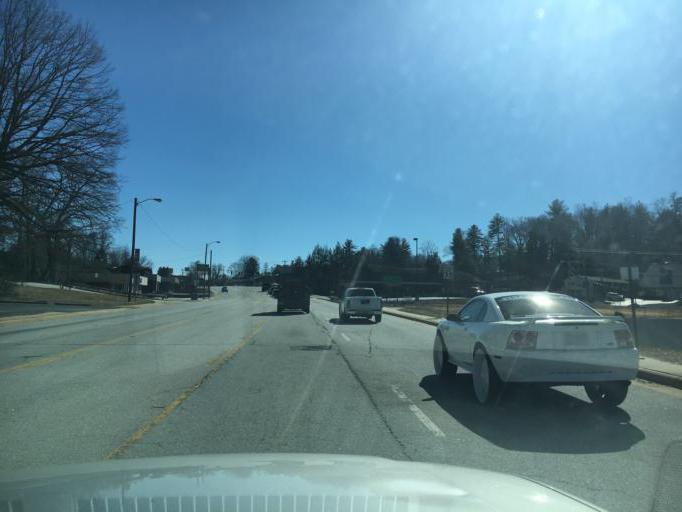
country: US
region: North Carolina
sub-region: Henderson County
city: Hendersonville
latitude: 35.3289
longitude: -82.4683
